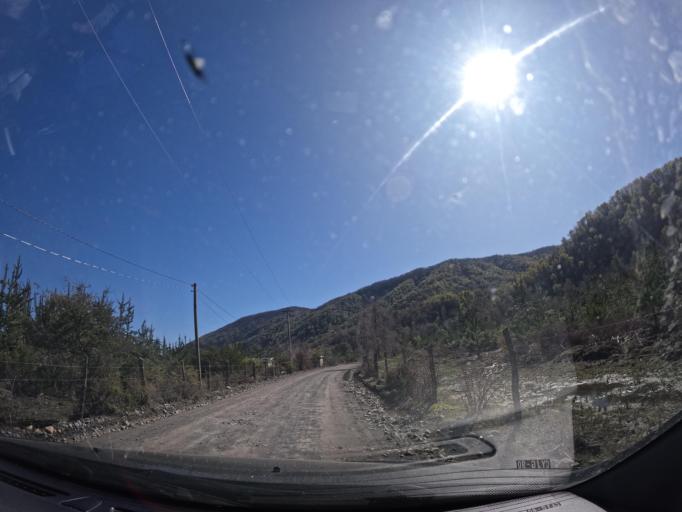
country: CL
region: Maule
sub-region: Provincia de Linares
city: Longavi
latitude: -36.2289
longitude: -71.3756
